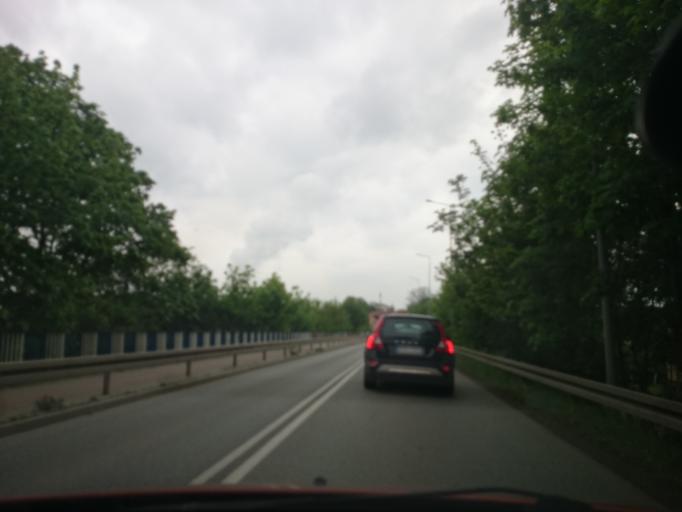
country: PL
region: Opole Voivodeship
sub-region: Powiat opolski
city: Czarnowasy
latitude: 50.7175
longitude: 17.9028
